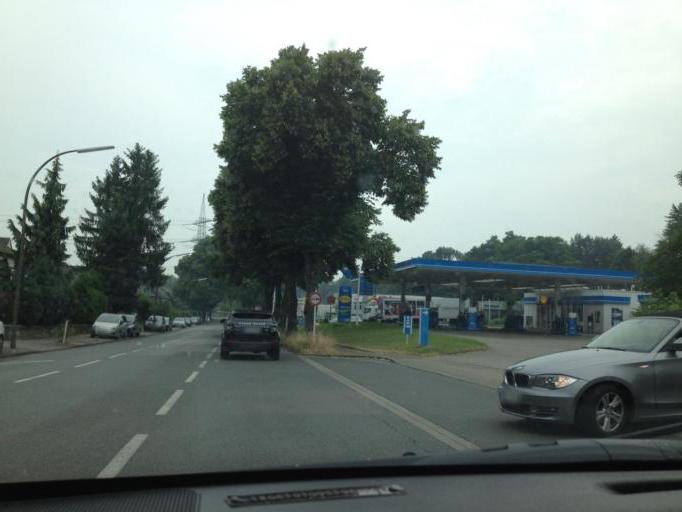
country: DE
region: North Rhine-Westphalia
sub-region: Regierungsbezirk Arnsberg
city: Dortmund
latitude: 51.4669
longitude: 7.4593
